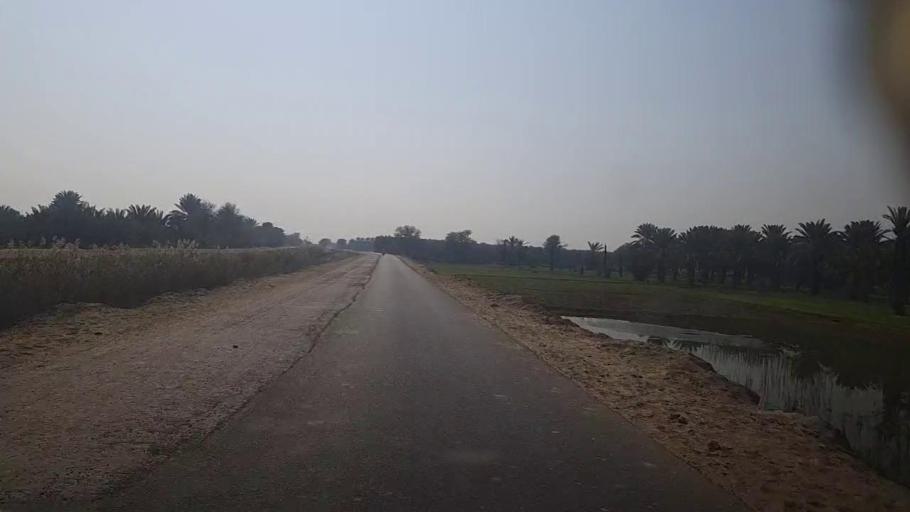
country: PK
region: Sindh
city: Khairpur
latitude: 27.4675
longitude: 68.8192
